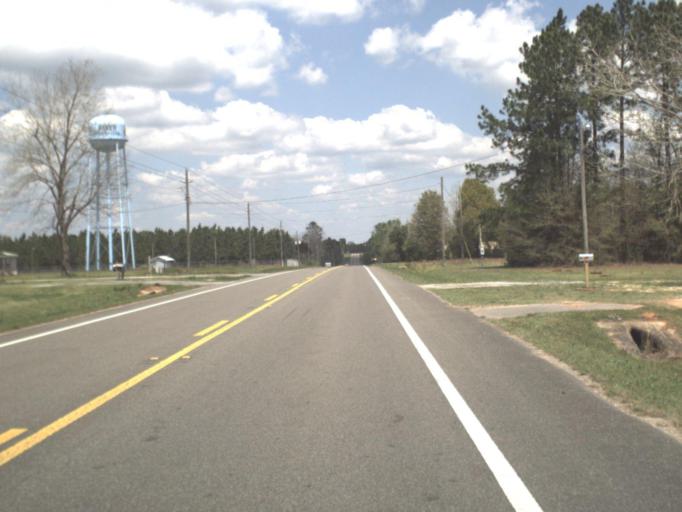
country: US
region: Florida
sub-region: Okaloosa County
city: Crestview
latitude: 30.8430
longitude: -86.6752
